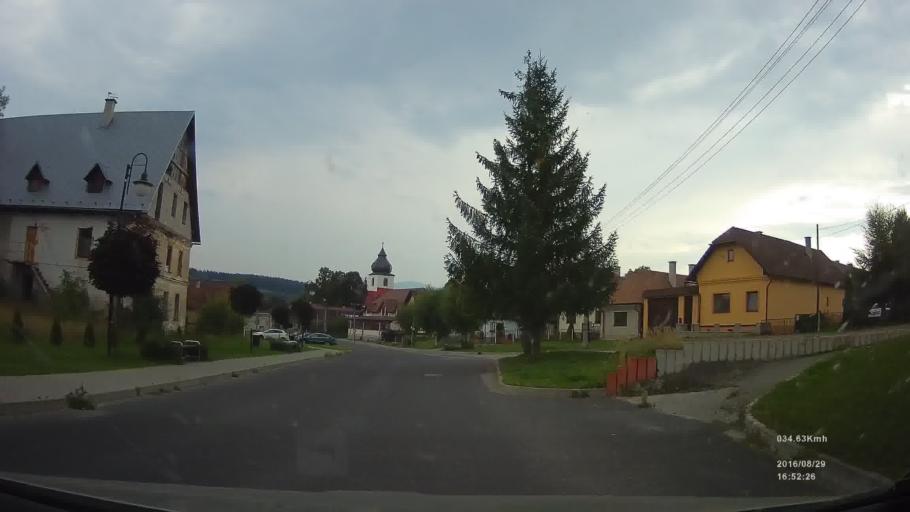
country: SK
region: Zilinsky
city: Ruzomberok
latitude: 49.1022
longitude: 19.4091
